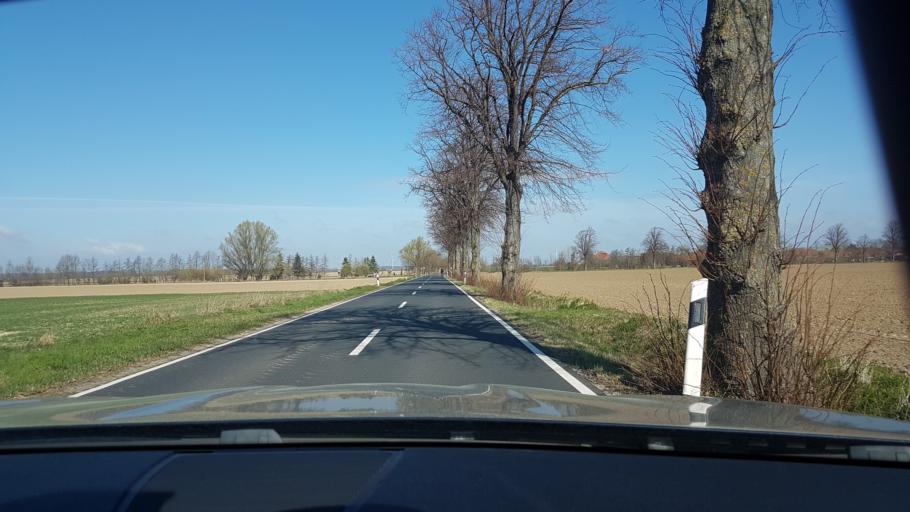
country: DE
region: Lower Saxony
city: Pattensen
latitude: 52.2365
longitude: 9.7263
